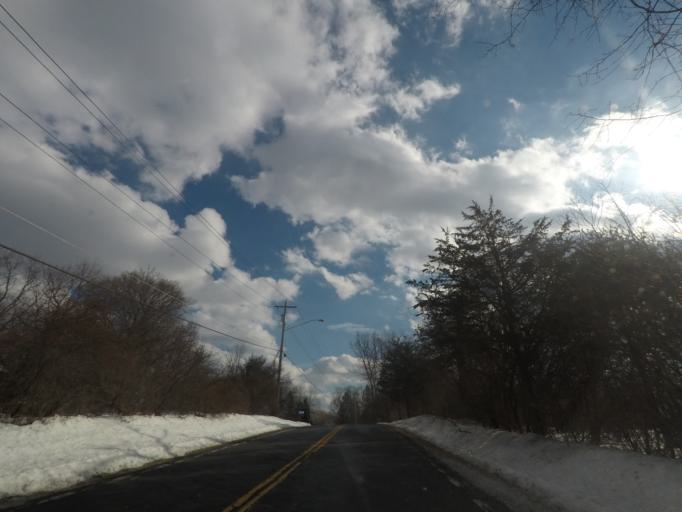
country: US
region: New York
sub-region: Schenectady County
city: Niskayuna
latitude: 42.8342
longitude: -73.8683
